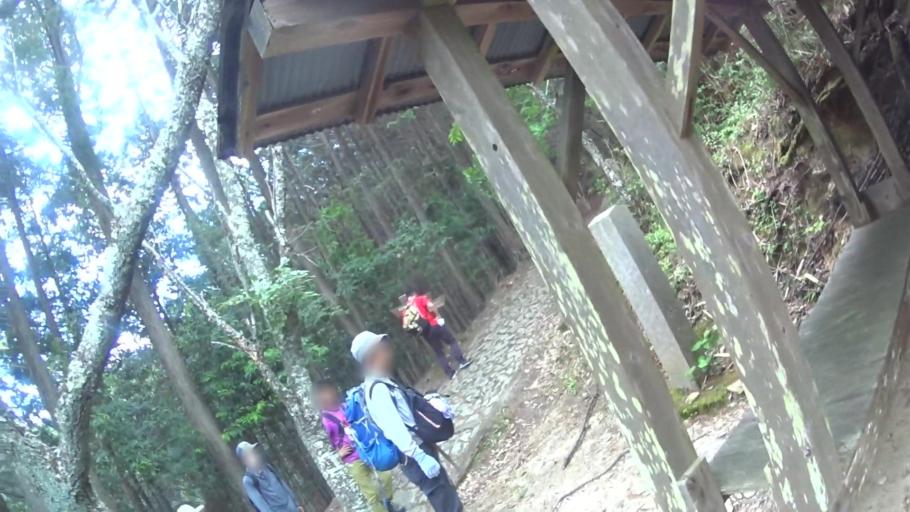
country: JP
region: Nara
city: Yoshino-cho
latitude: 34.3602
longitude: 135.8712
